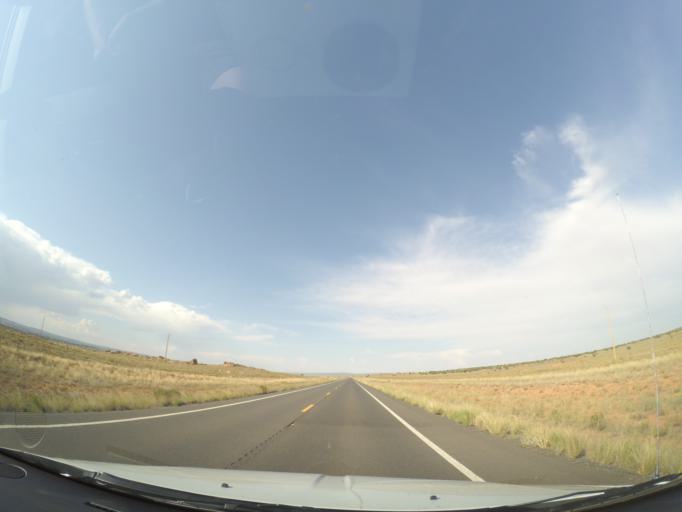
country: US
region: Arizona
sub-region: Coconino County
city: Tuba City
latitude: 36.3494
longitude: -111.4261
